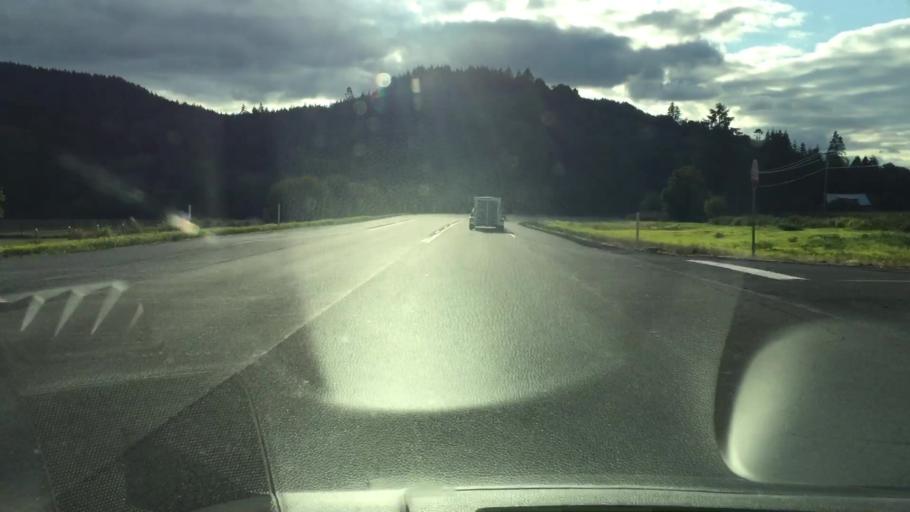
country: US
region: Washington
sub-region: Lewis County
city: Morton
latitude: 46.5323
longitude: -122.5327
